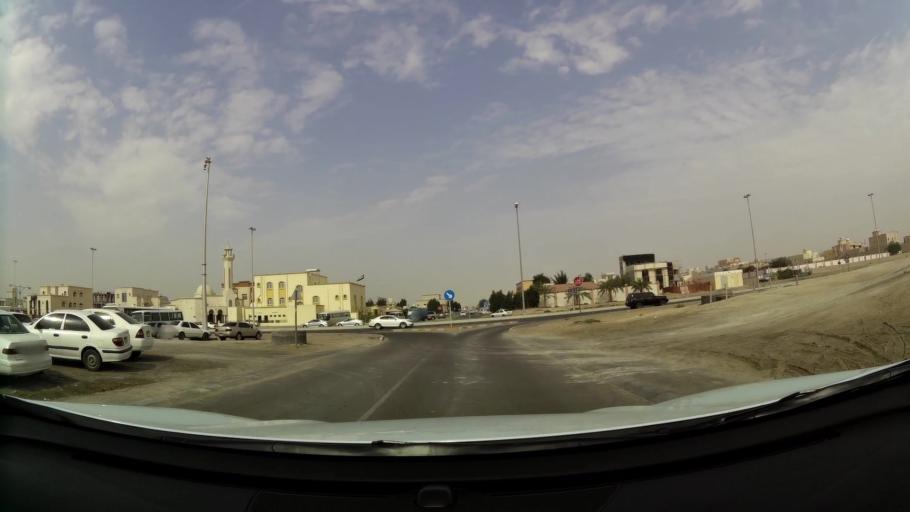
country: AE
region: Abu Dhabi
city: Abu Dhabi
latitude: 24.2896
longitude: 54.6564
